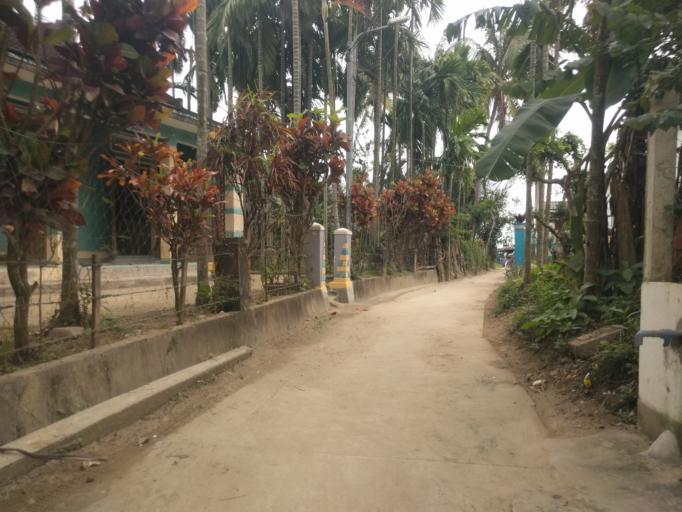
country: VN
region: Quang Nam
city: Hoi An
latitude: 15.8694
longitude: 108.3530
